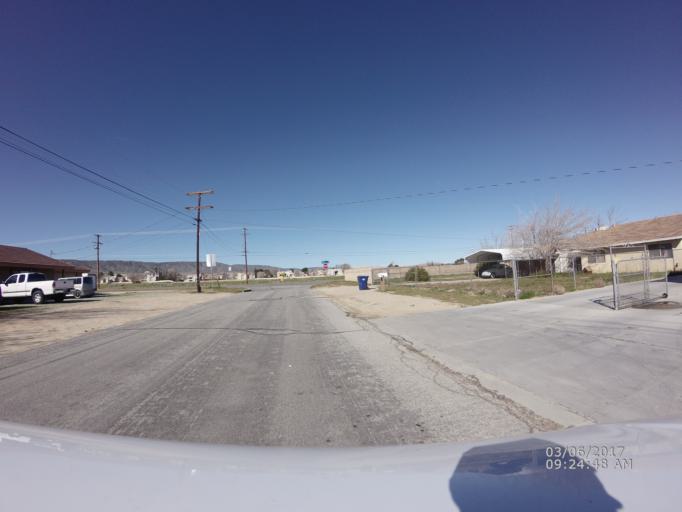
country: US
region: California
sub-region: Los Angeles County
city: Quartz Hill
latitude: 34.6548
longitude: -118.2181
